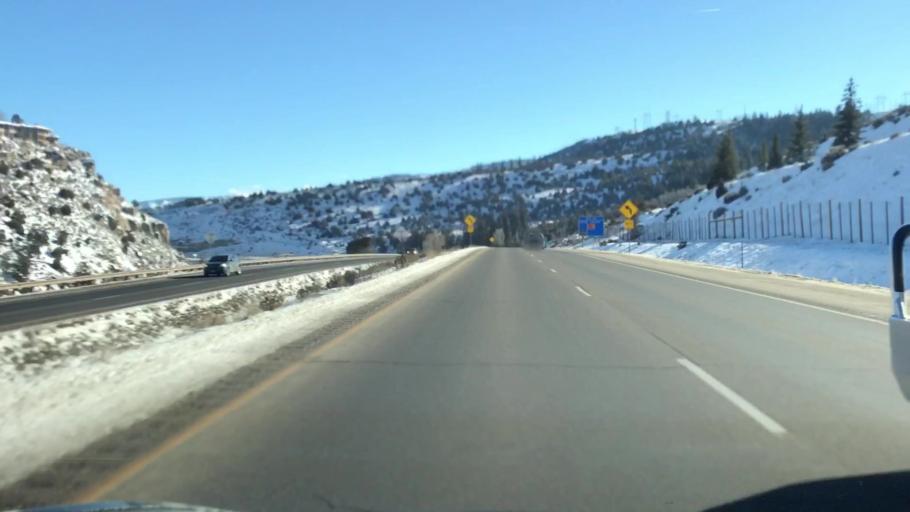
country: US
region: Colorado
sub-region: Eagle County
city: Edwards
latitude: 39.7060
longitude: -106.6909
